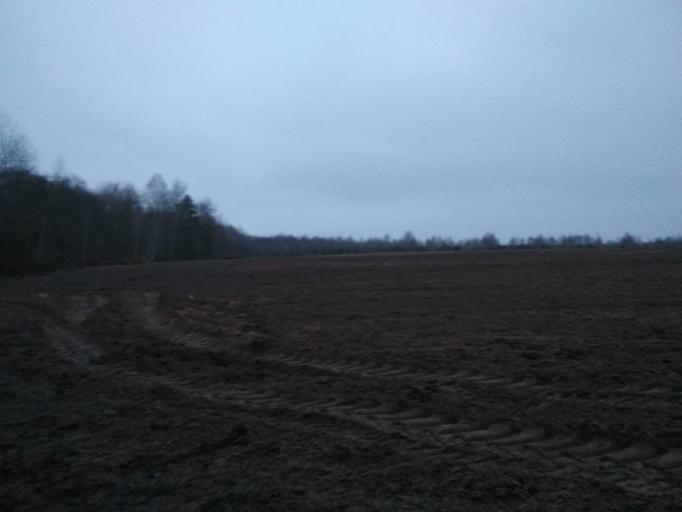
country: BY
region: Minsk
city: Mar''ina Horka
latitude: 53.4780
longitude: 28.1703
